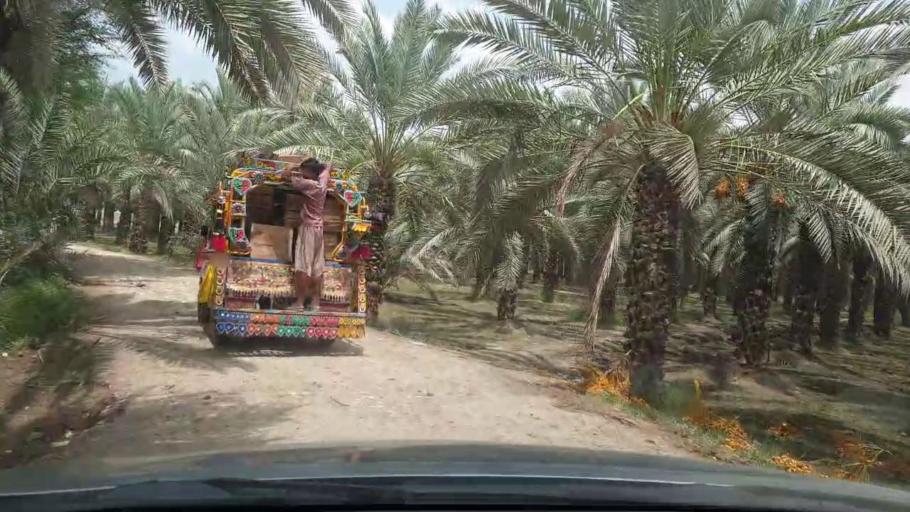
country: PK
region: Sindh
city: Kot Diji
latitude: 27.4204
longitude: 68.7643
